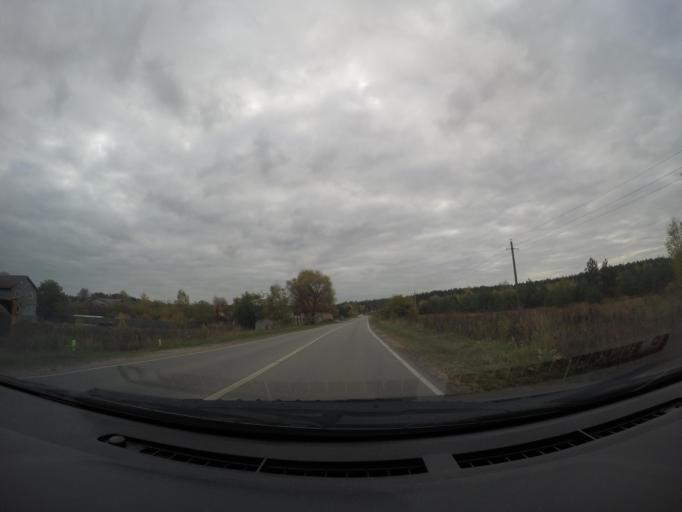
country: RU
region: Moskovskaya
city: Gzhel'
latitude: 55.6417
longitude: 38.4117
